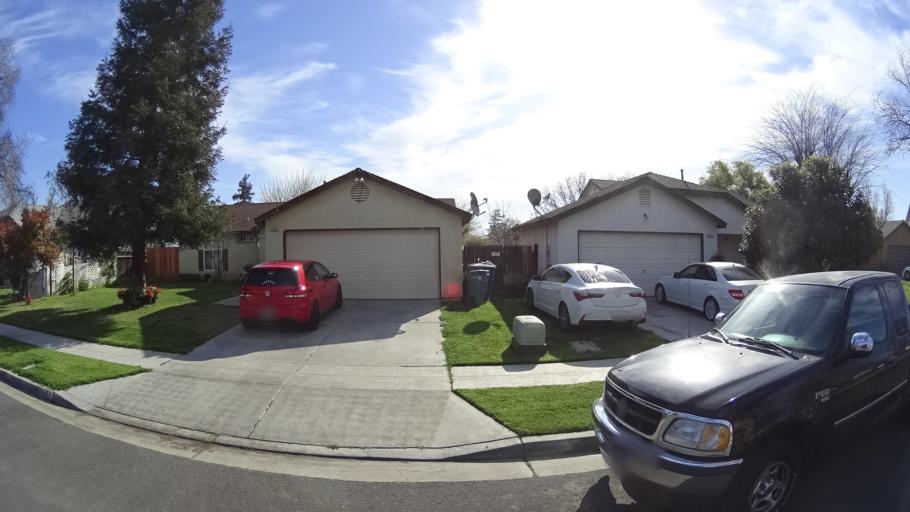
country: US
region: California
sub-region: Fresno County
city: West Park
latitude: 36.8032
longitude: -119.8923
